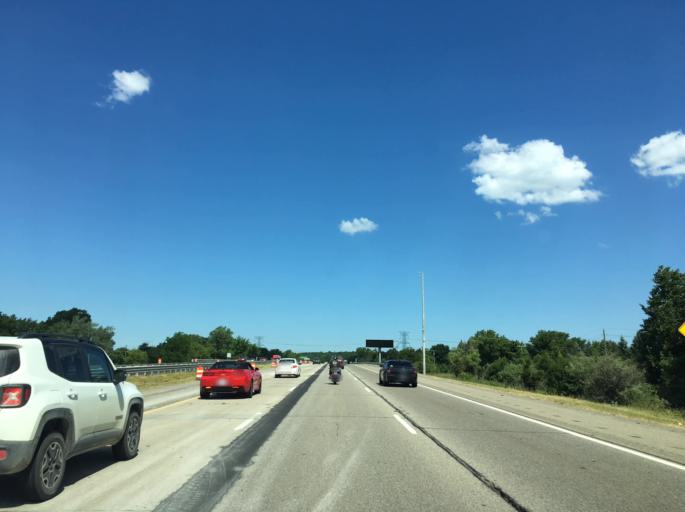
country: US
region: Michigan
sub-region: Oakland County
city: Waterford
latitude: 42.7194
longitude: -83.3469
